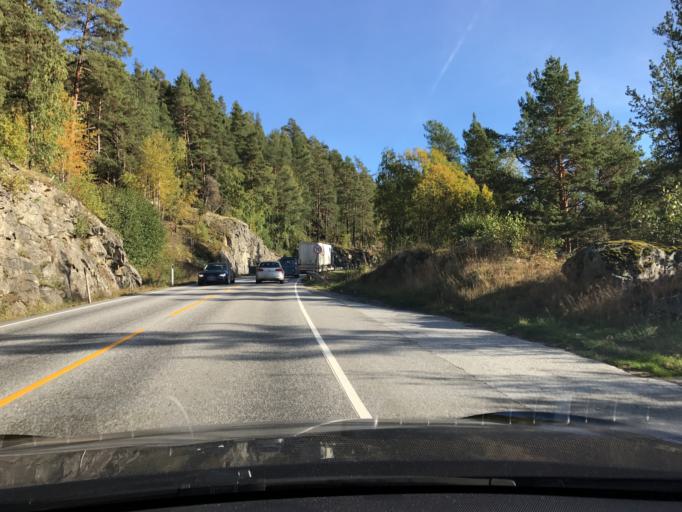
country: NO
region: Sogn og Fjordane
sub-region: Sogndal
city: Sogndalsfjora
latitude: 61.2129
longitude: 7.1410
